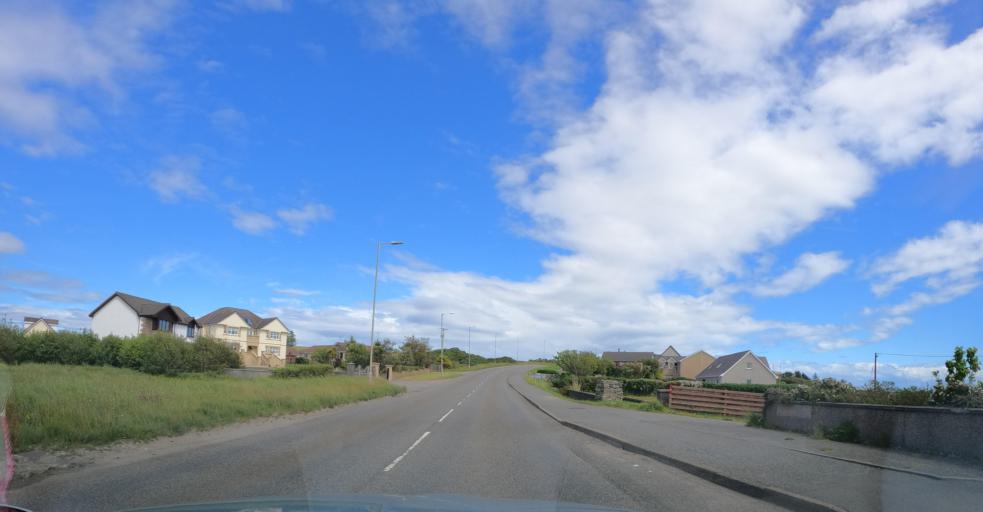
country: GB
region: Scotland
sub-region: Eilean Siar
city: Stornoway
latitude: 58.2082
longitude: -6.3636
